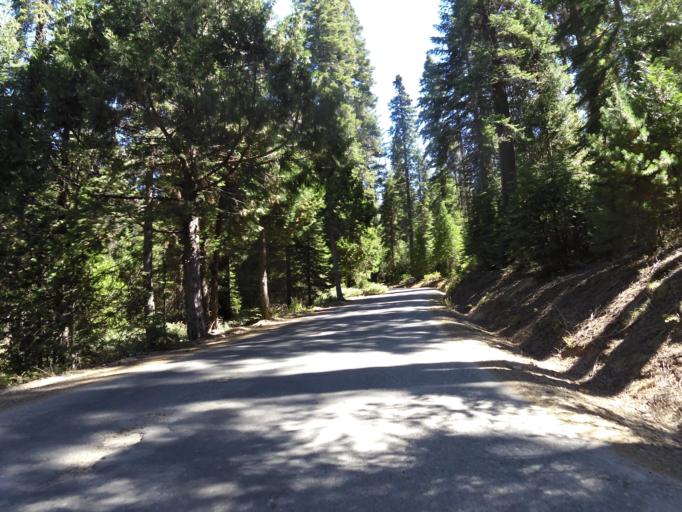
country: US
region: California
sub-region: Madera County
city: Oakhurst
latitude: 37.4271
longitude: -119.5523
